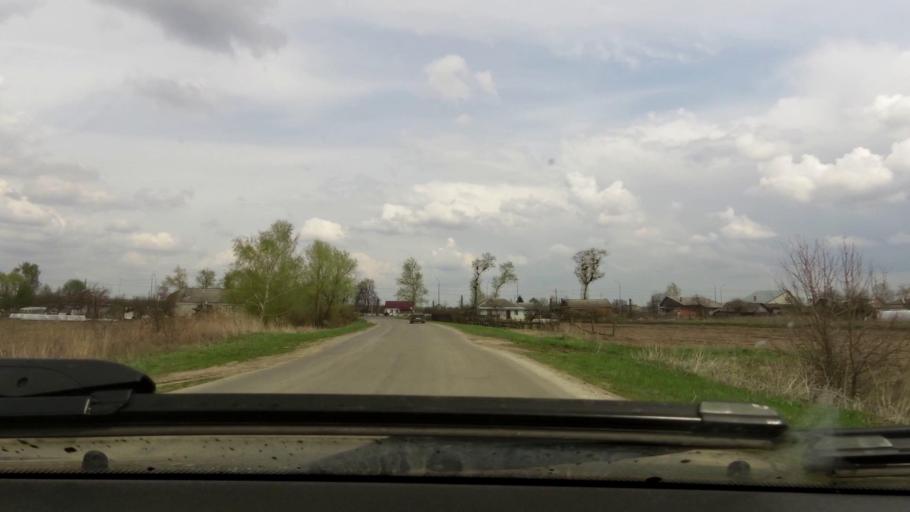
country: RU
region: Rjazan
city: Bagramovo
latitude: 54.7502
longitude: 39.4213
